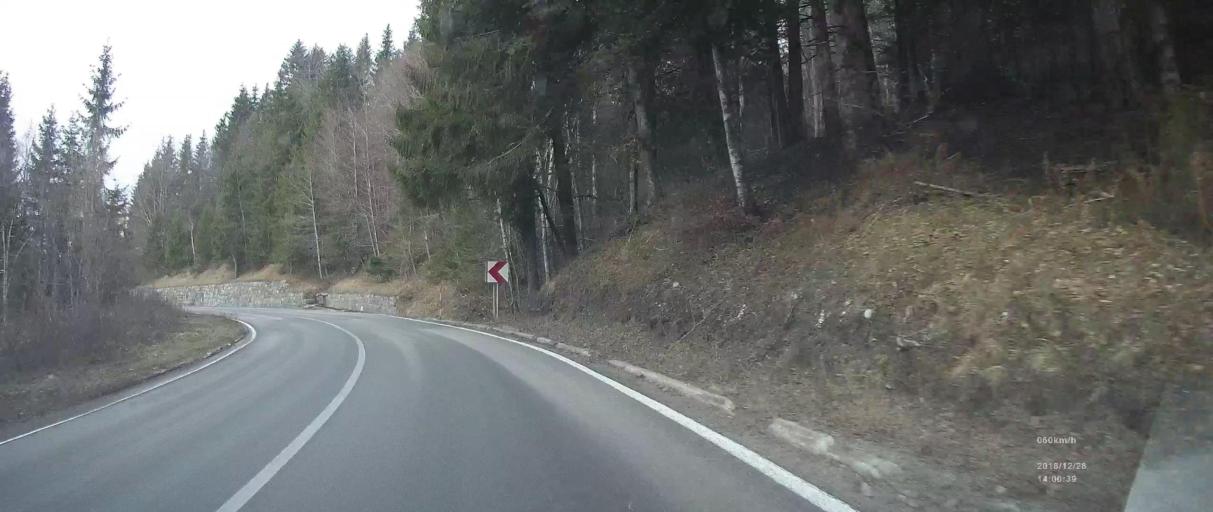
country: SI
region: Kostel
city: Kostel
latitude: 45.4140
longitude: 14.9141
